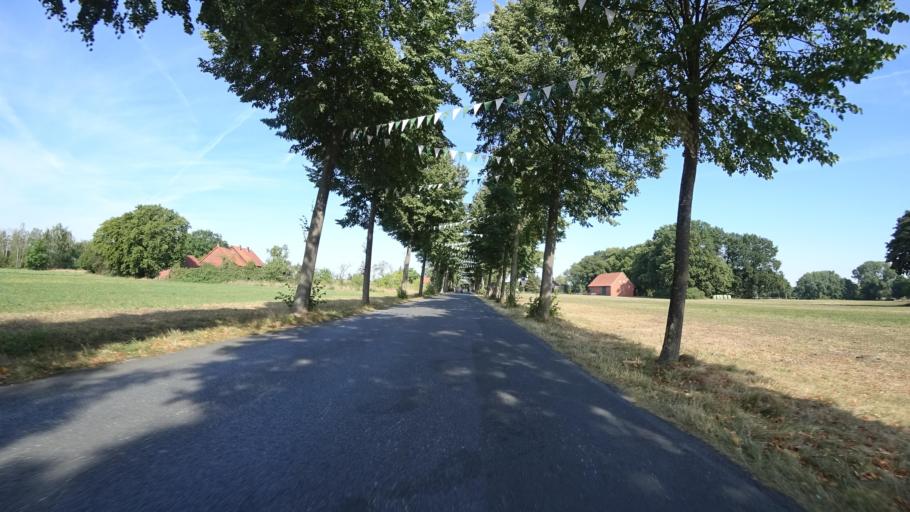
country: DE
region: North Rhine-Westphalia
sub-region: Regierungsbezirk Detmold
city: Rheda-Wiedenbruck
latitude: 51.8636
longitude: 8.2793
